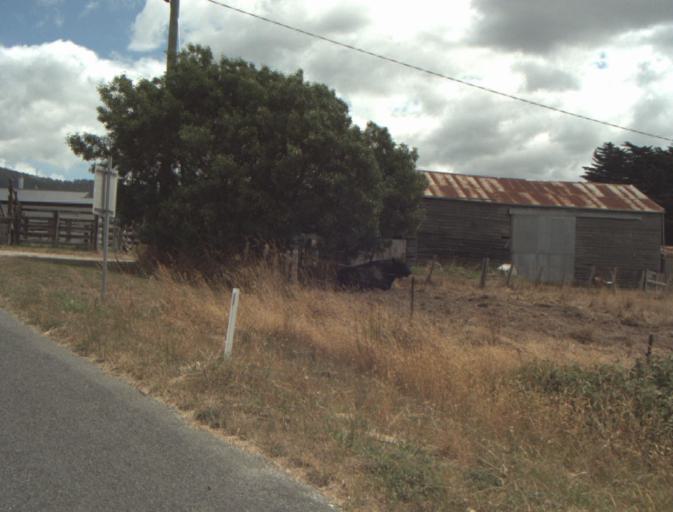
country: AU
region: Tasmania
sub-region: Launceston
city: Mayfield
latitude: -41.2375
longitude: 147.1487
